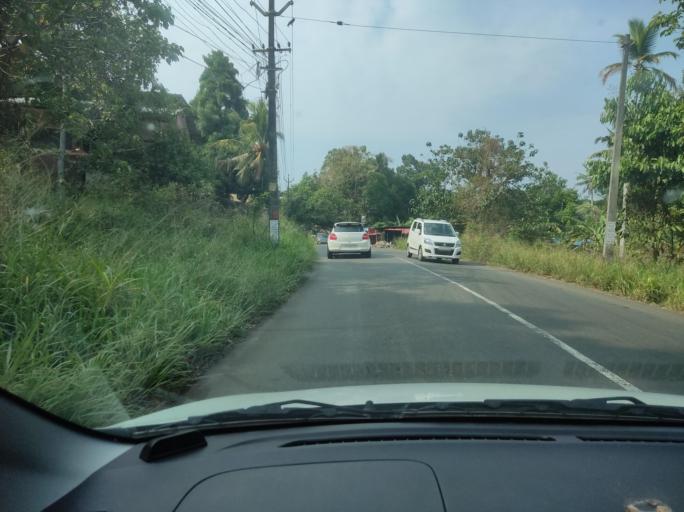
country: IN
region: Kerala
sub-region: Pattanamtitta
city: Adur
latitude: 9.1395
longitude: 76.7302
